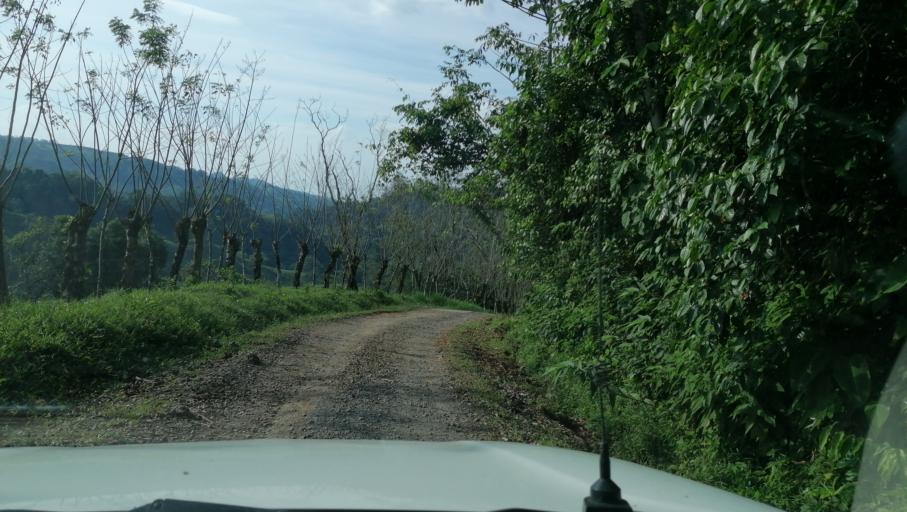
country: MX
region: Chiapas
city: Ostuacan
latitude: 17.4680
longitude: -93.2340
